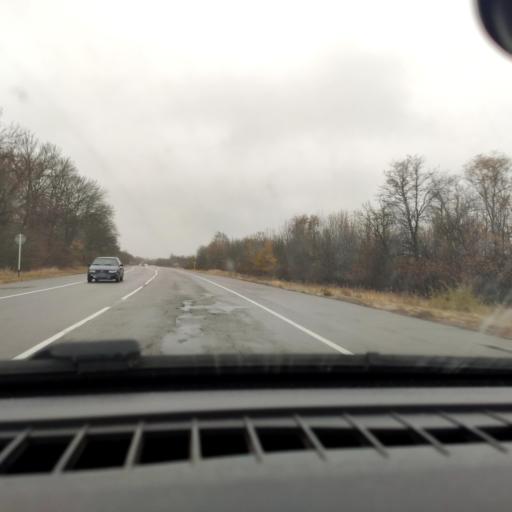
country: RU
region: Voronezj
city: Kolodeznyy
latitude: 51.3078
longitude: 39.0374
